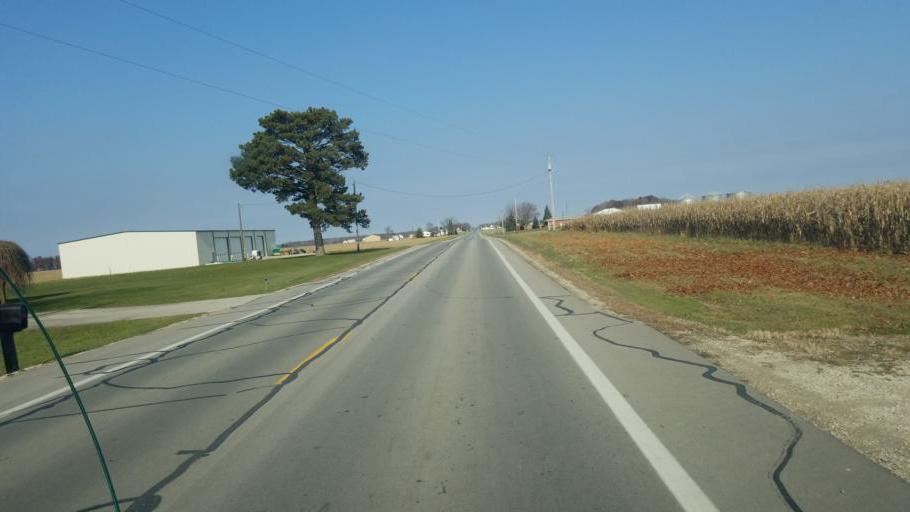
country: US
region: Ohio
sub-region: Mercer County
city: Coldwater
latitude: 40.5115
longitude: -84.6286
